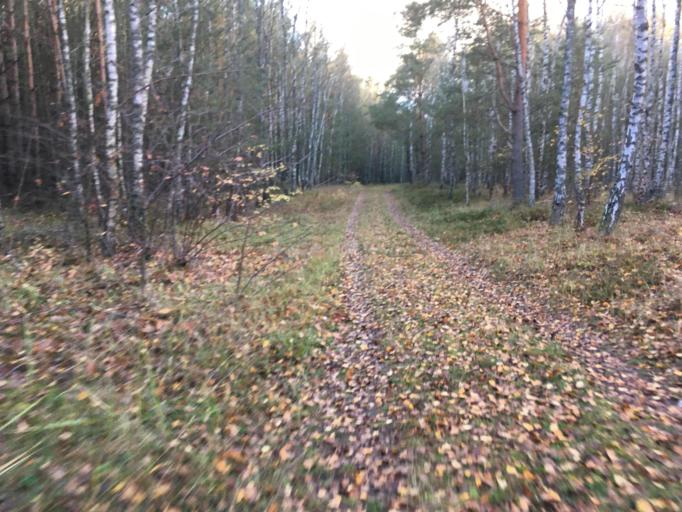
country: DE
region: Brandenburg
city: Birkenwerder
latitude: 52.7020
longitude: 13.3429
